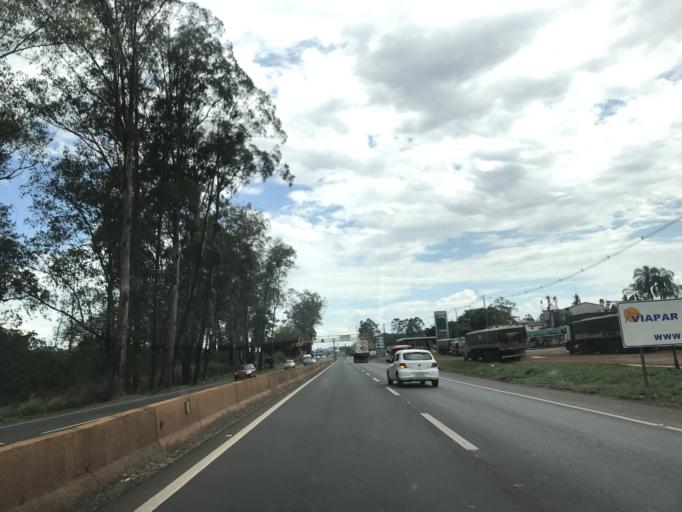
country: BR
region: Parana
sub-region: Rolandia
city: Rolandia
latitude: -23.3550
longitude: -51.3925
